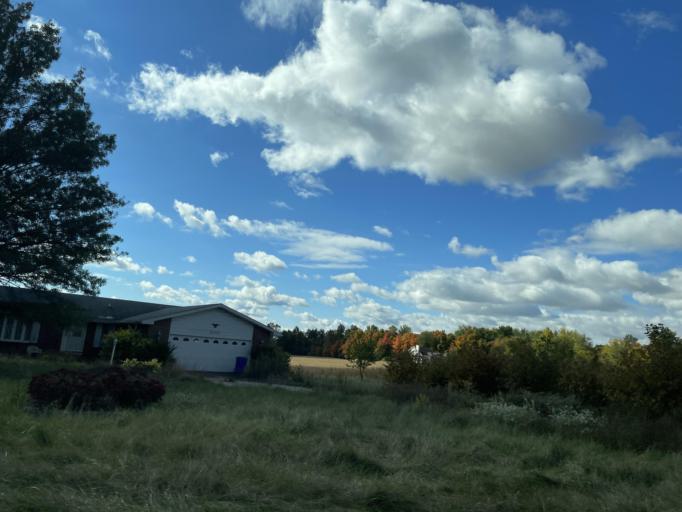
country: US
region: Indiana
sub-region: Allen County
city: Fort Wayne
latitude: 41.1145
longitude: -85.2291
